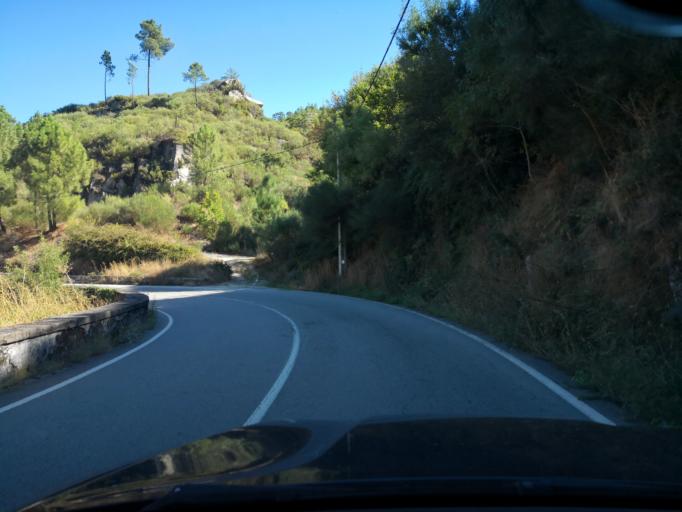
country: PT
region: Vila Real
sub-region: Vila Real
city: Vila Real
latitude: 41.2667
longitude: -7.7809
